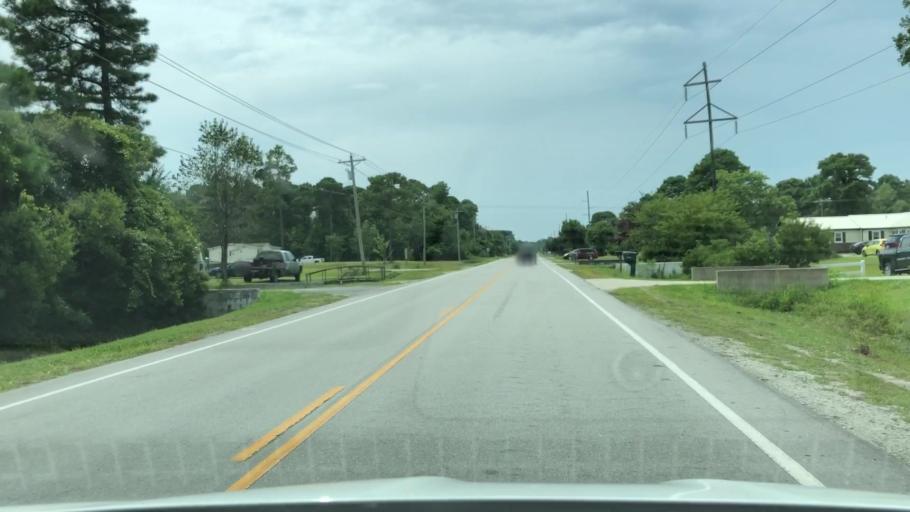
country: US
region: North Carolina
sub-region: Carteret County
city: Newport
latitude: 34.7428
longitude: -76.8829
